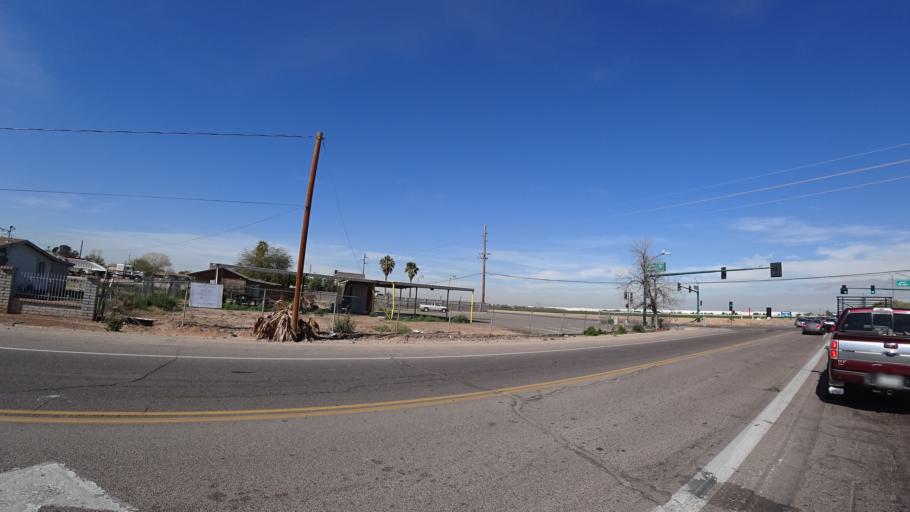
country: US
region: Arizona
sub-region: Maricopa County
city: Tolleson
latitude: 33.4222
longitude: -112.2040
